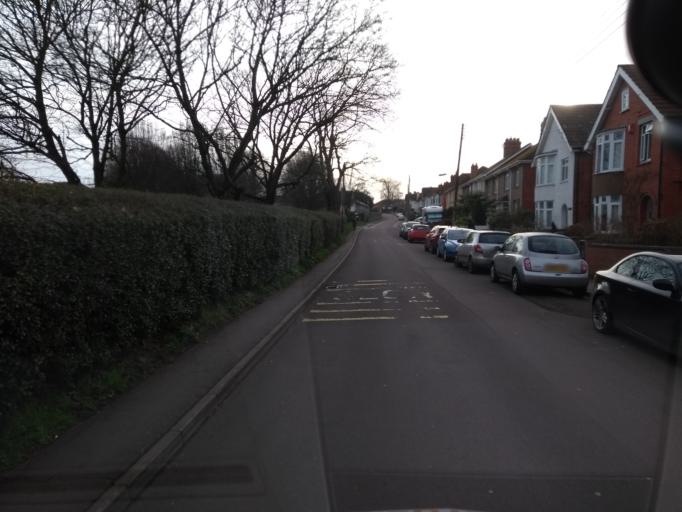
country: GB
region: England
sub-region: Somerset
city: Street
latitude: 51.1261
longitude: -2.7349
